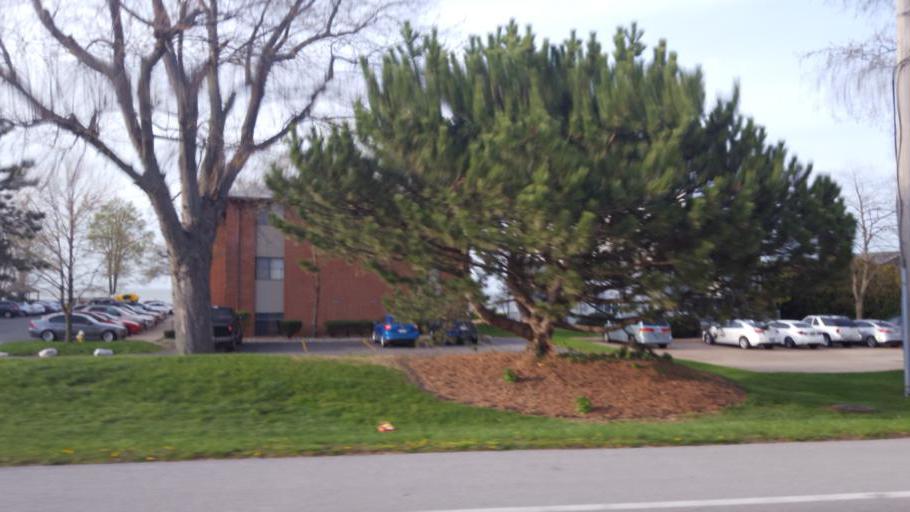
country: US
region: Ohio
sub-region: Erie County
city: Huron
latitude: 41.4074
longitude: -82.5731
